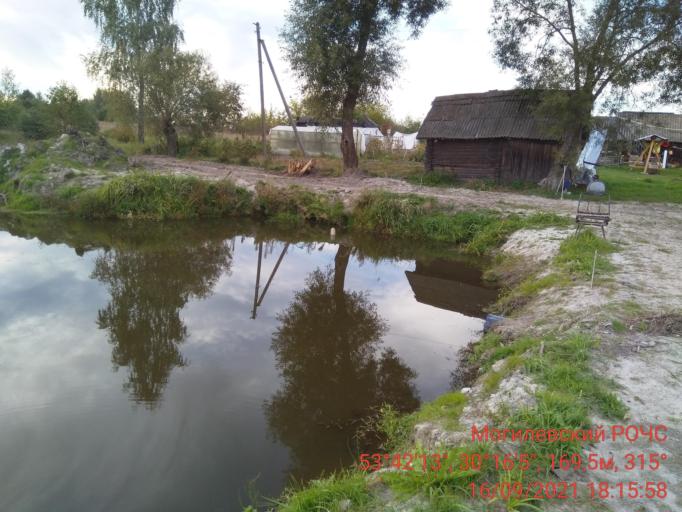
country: BY
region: Mogilev
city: Dashkawka
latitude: 53.7036
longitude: 30.2682
